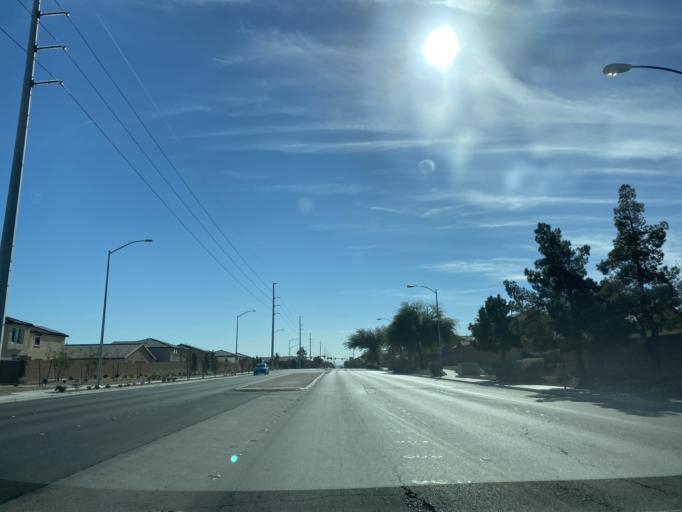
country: US
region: Nevada
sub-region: Clark County
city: North Las Vegas
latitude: 36.2641
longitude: -115.1440
